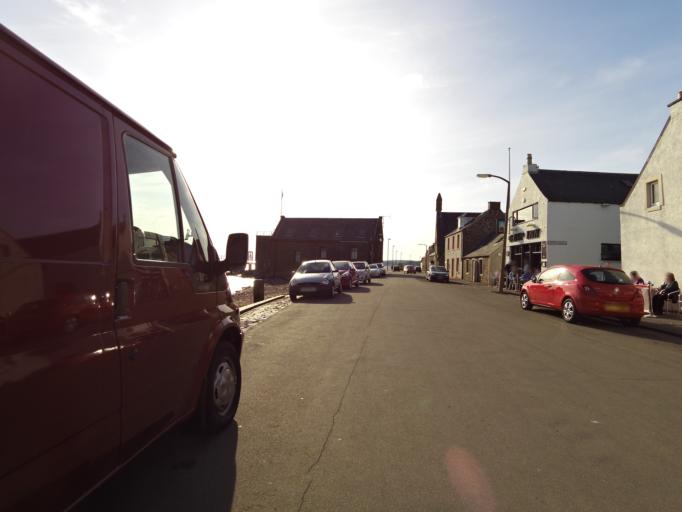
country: GB
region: Scotland
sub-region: Fife
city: Tayport
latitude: 56.4650
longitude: -2.8764
